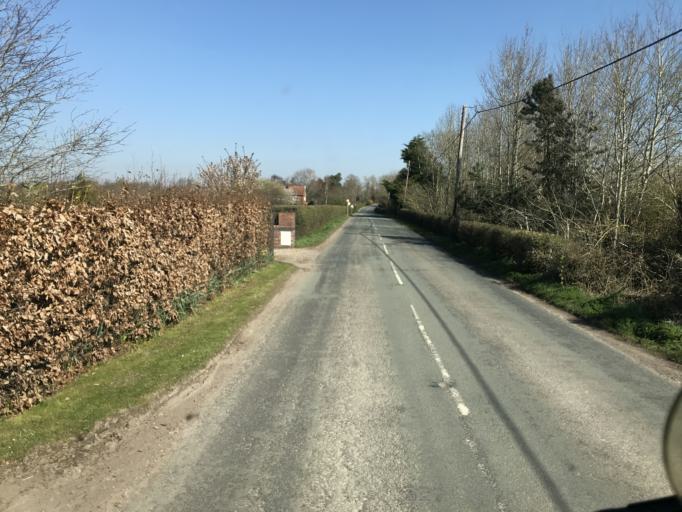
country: GB
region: England
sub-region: Cheshire West and Chester
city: Waverton
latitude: 53.1632
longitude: -2.8258
